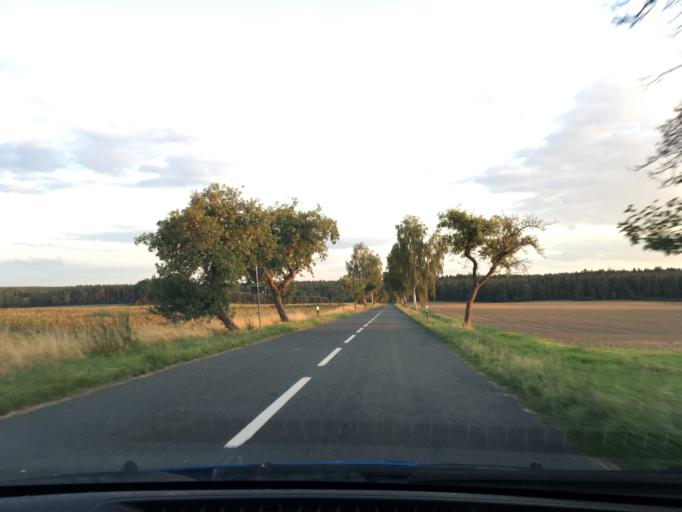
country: DE
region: Lower Saxony
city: Tosterglope
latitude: 53.2066
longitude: 10.8173
